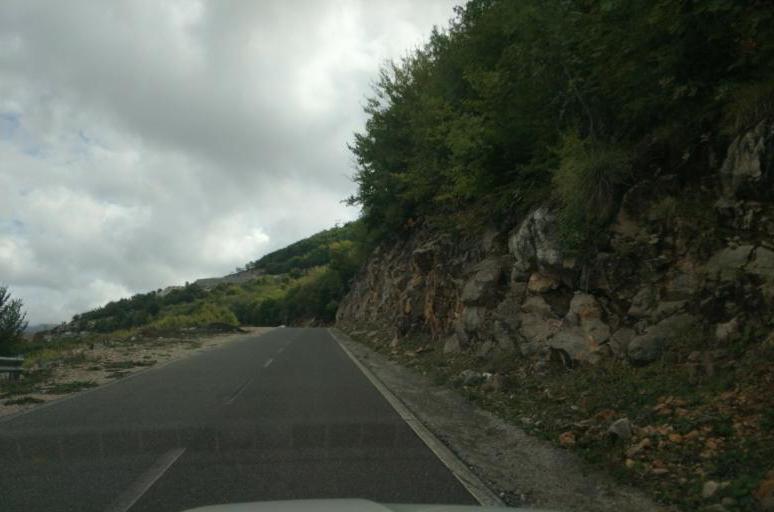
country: AL
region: Durres
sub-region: Rrethi i Krujes
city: Kruje
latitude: 41.5237
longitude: 19.8037
